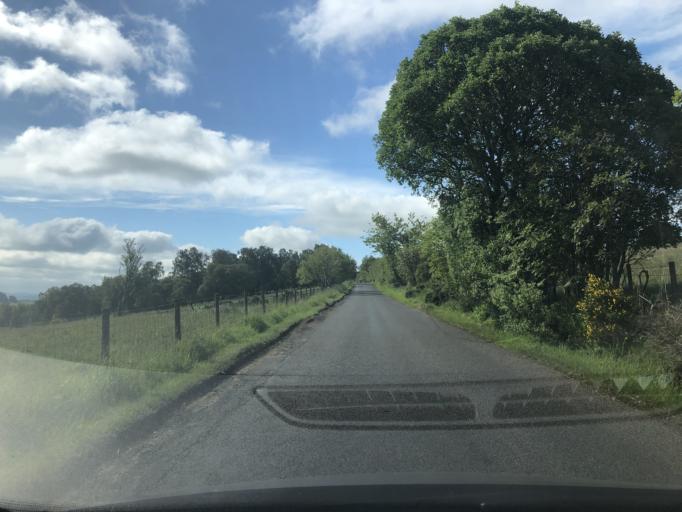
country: GB
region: Scotland
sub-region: Angus
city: Kirriemuir
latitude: 56.7488
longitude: -3.0139
